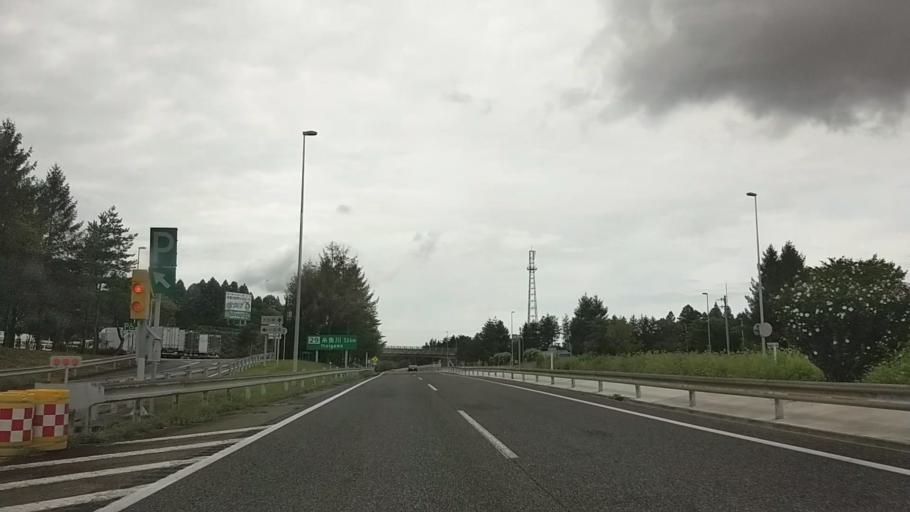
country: JP
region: Niigata
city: Itoigawa
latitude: 37.0332
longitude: 137.8711
